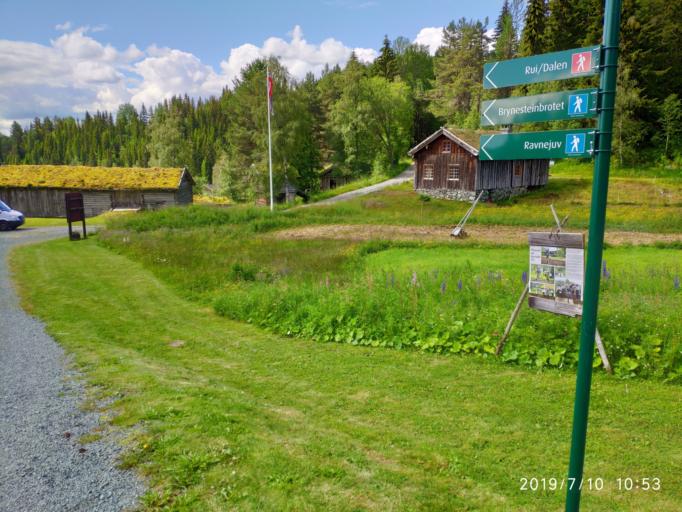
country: NO
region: Telemark
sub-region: Tokke
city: Dalen
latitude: 59.4657
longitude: 8.0198
